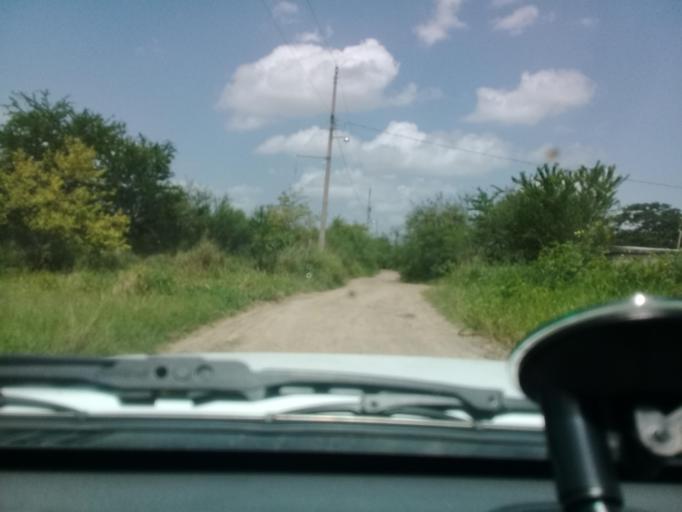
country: MX
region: Veracruz
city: Moralillo
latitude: 22.1816
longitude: -98.0175
